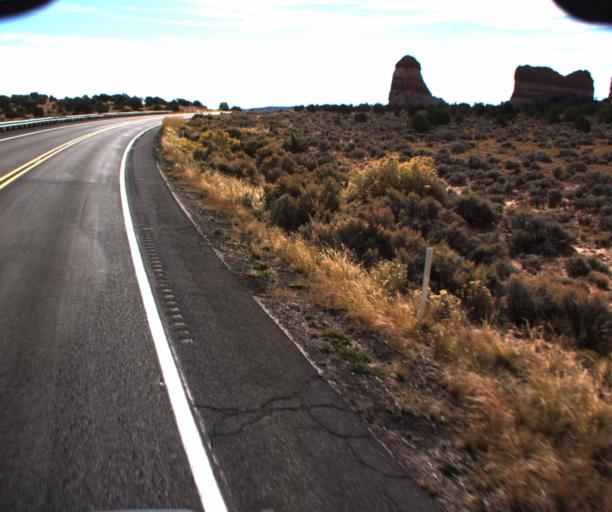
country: US
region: Arizona
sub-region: Coconino County
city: Kaibito
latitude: 36.6138
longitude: -110.9255
